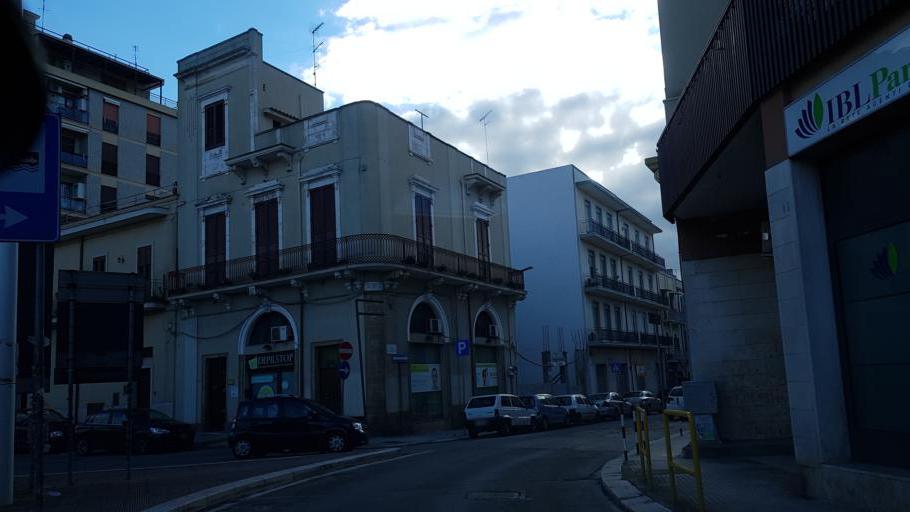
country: IT
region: Apulia
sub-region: Provincia di Brindisi
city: Brindisi
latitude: 40.6381
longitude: 17.9377
